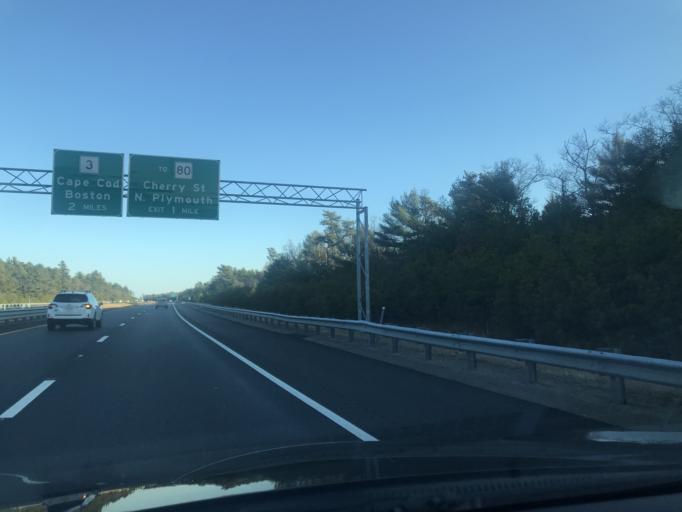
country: US
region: Massachusetts
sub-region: Plymouth County
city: Kingston
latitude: 41.9607
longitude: -70.7339
